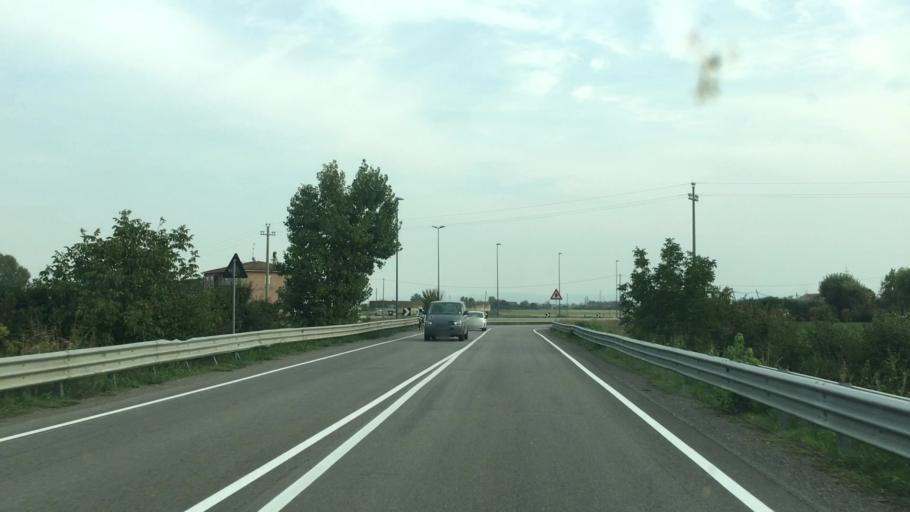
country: IT
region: Emilia-Romagna
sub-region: Provincia di Reggio Emilia
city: Caprara
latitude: 44.7667
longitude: 10.5002
